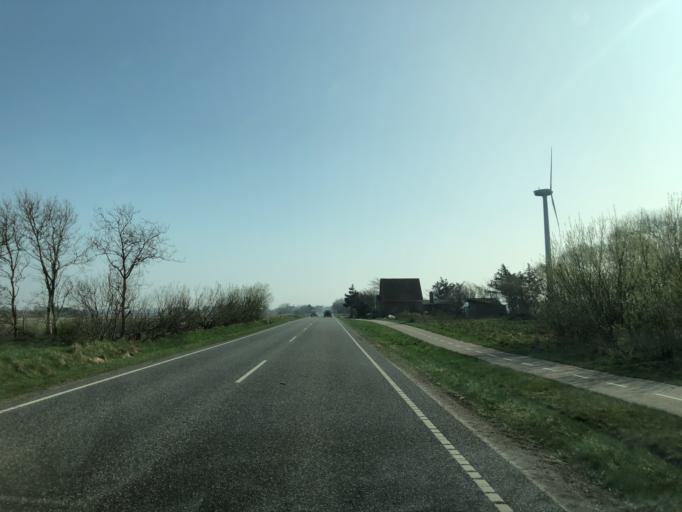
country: DK
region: South Denmark
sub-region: Varde Kommune
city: Oksbol
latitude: 55.8183
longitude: 8.3064
